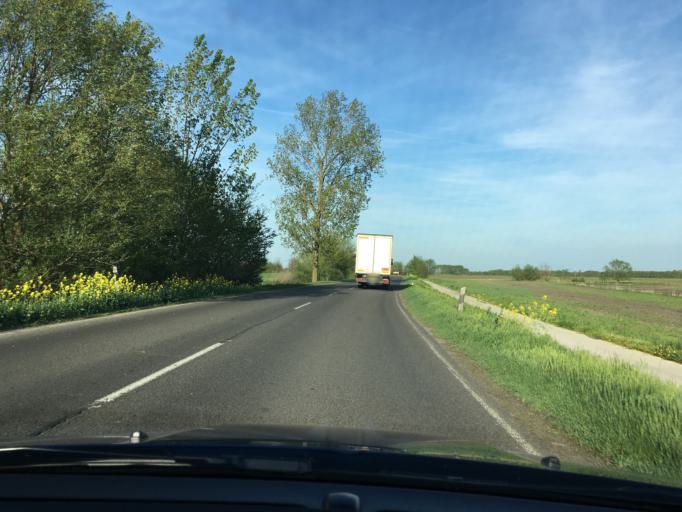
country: HU
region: Bekes
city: Korosladany
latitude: 47.0042
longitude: 21.1204
